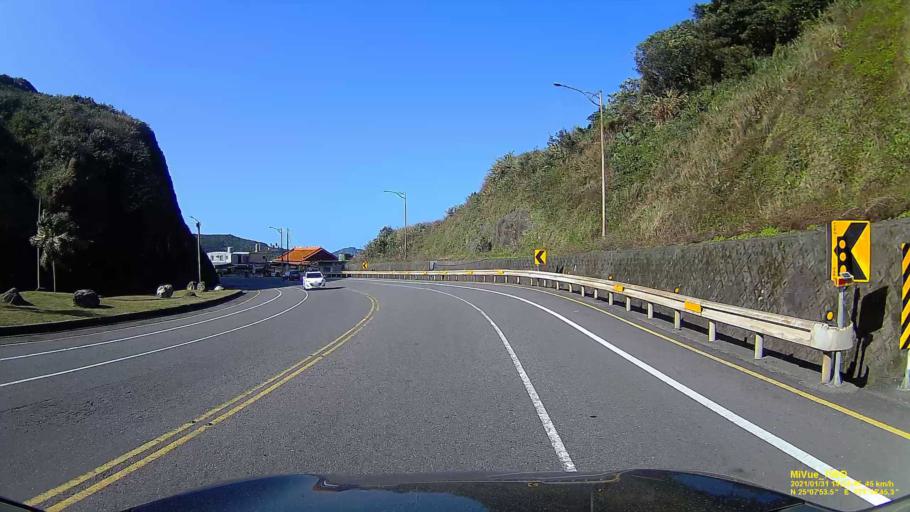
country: TW
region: Taiwan
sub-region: Keelung
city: Keelung
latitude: 25.1317
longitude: 121.8125
